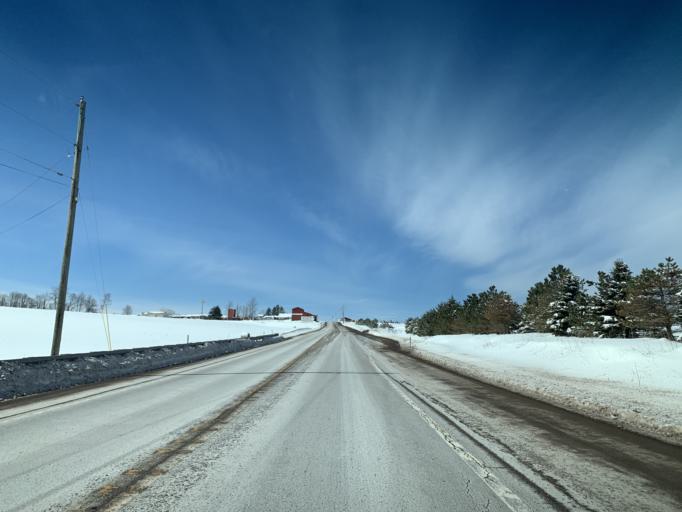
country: US
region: Pennsylvania
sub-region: Somerset County
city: Meyersdale
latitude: 39.6952
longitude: -79.2362
